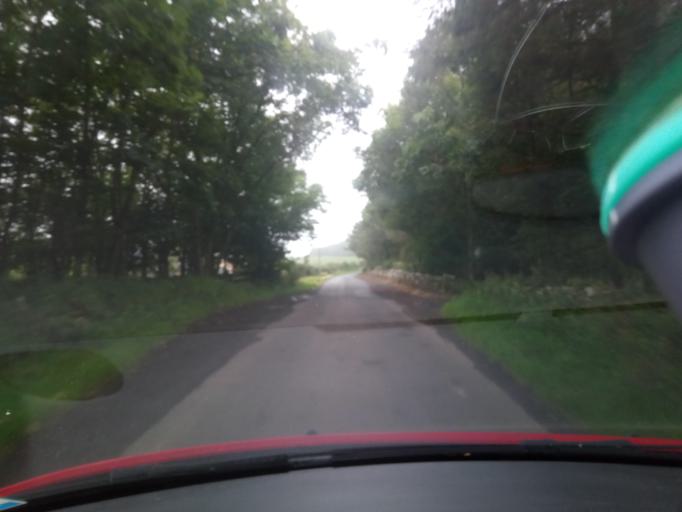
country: GB
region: Scotland
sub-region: The Scottish Borders
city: Earlston
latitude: 55.6493
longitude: -2.7156
